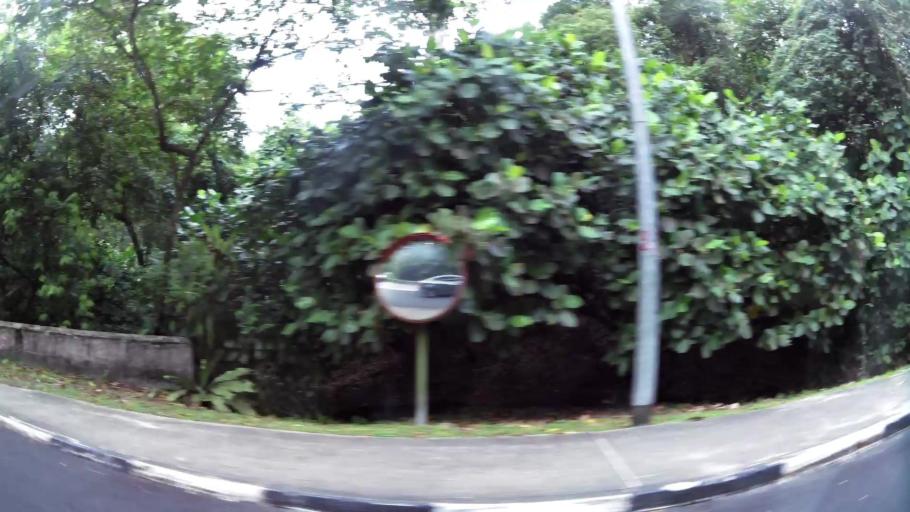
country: SG
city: Singapore
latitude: 1.2871
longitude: 103.7857
